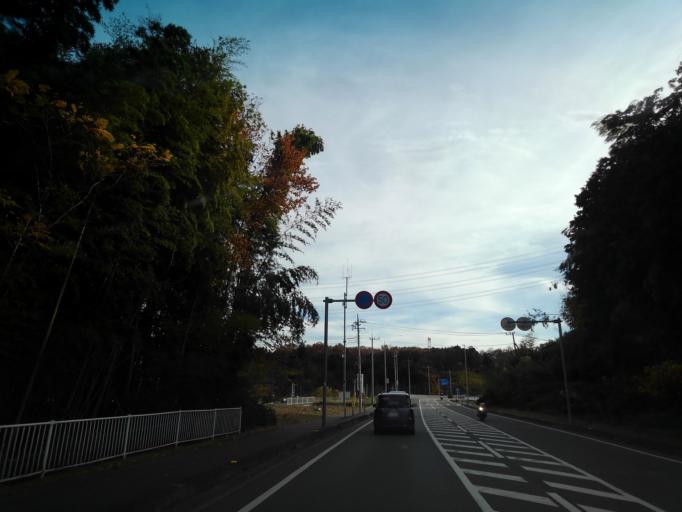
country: JP
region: Saitama
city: Morohongo
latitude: 35.9276
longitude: 139.3202
